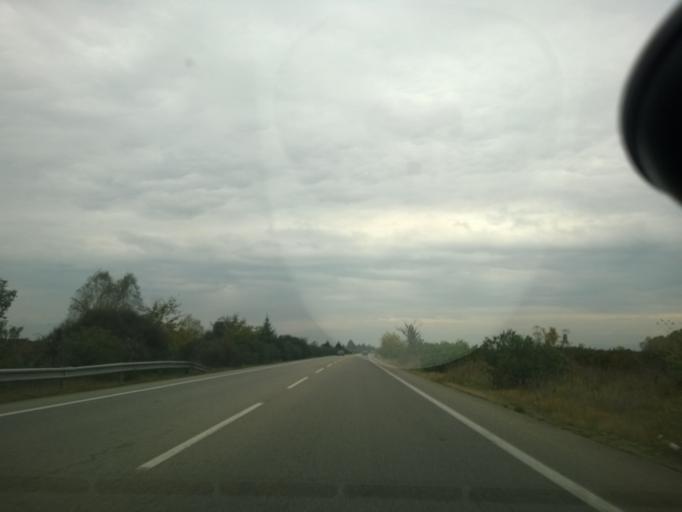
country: GR
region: Central Macedonia
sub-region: Nomos Pellis
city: Karyotissa
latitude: 40.7807
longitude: 22.3047
